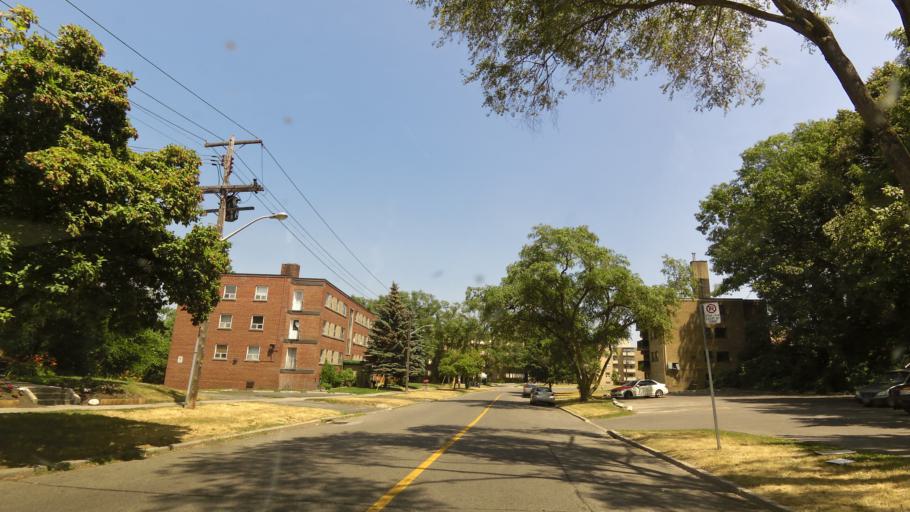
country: CA
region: Ontario
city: Etobicoke
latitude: 43.6400
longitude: -79.4915
